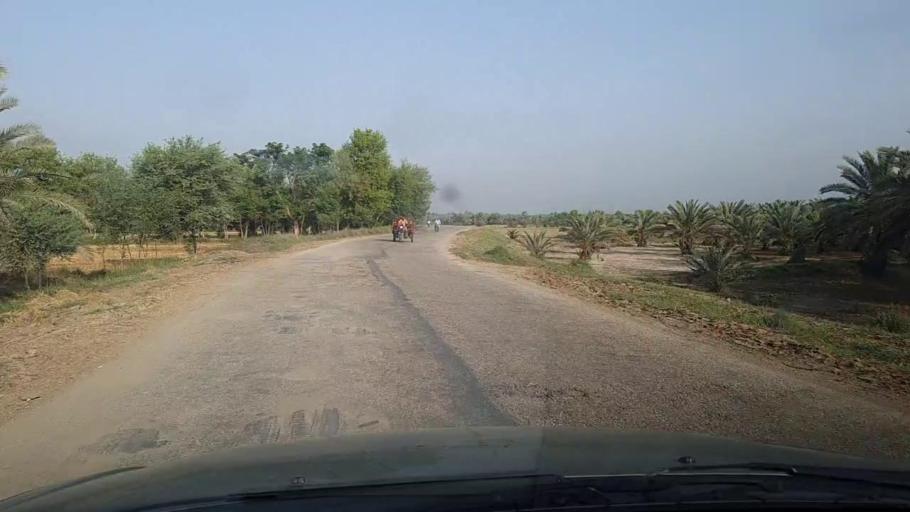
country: PK
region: Sindh
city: Pir jo Goth
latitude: 27.5623
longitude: 68.6593
